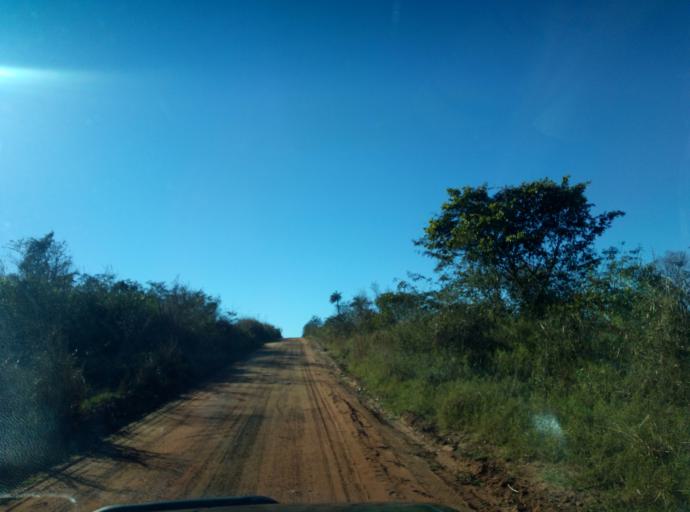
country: PY
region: Caaguazu
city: Doctor Cecilio Baez
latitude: -25.1591
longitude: -56.2884
